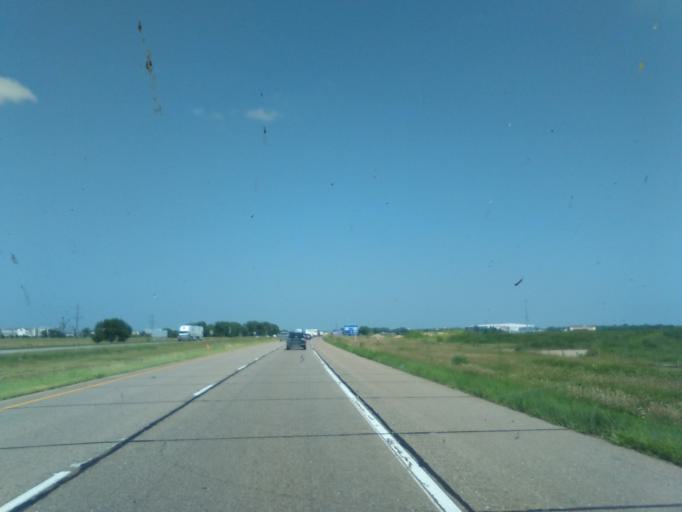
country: US
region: Nebraska
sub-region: Buffalo County
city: Kearney
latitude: 40.6702
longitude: -99.1051
